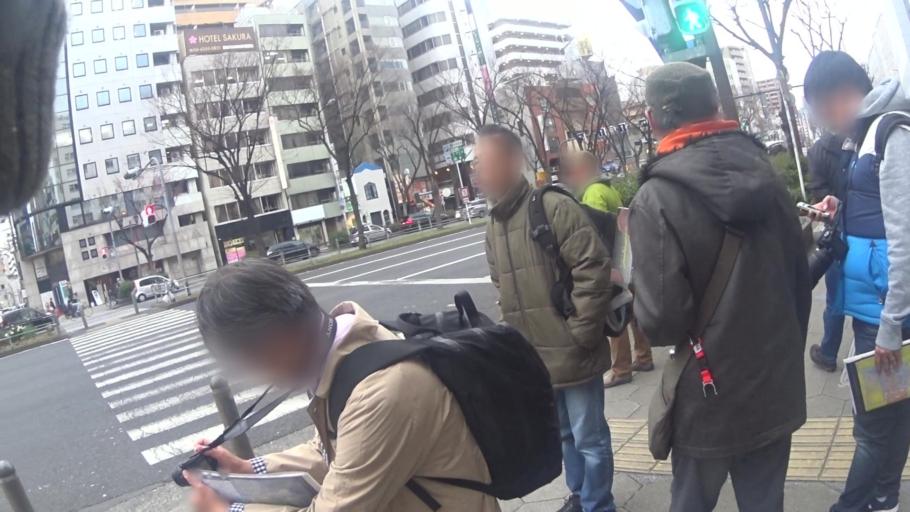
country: JP
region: Osaka
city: Osaka-shi
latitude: 34.6668
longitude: 135.5171
